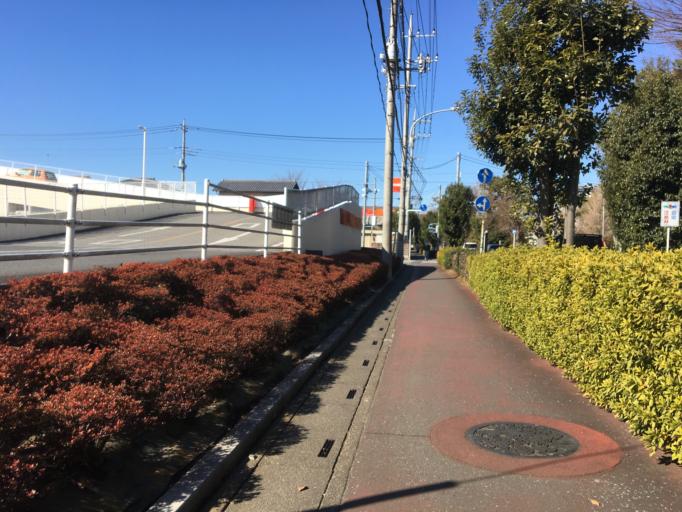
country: JP
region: Saitama
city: Oi
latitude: 35.8398
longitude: 139.5251
